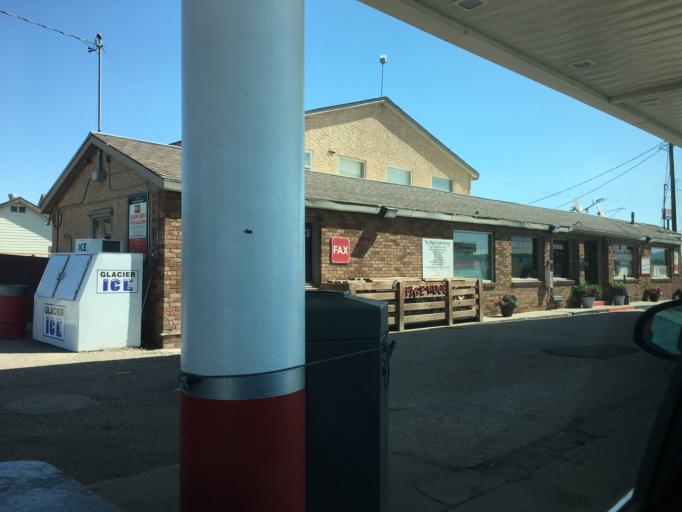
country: US
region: Wyoming
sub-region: Albany County
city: Laramie
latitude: 41.3092
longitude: -105.6178
